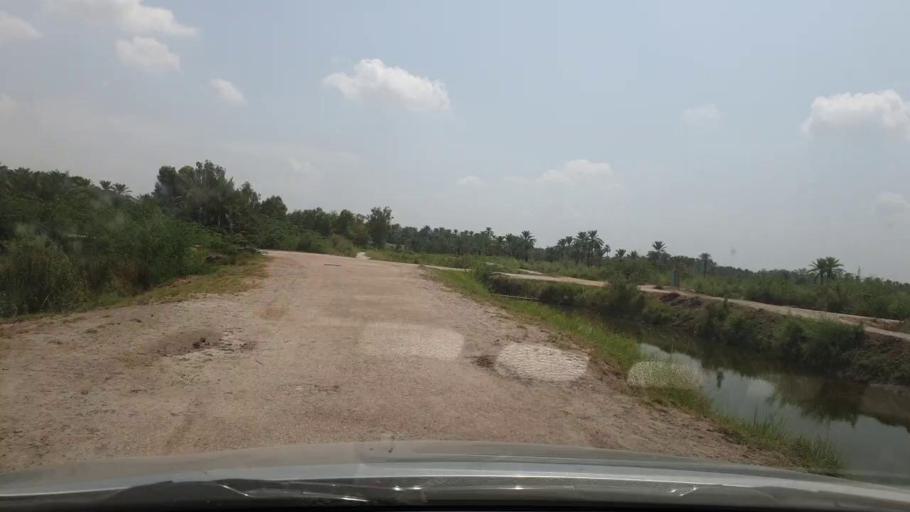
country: PK
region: Sindh
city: Kot Diji
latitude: 27.3752
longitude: 68.7095
